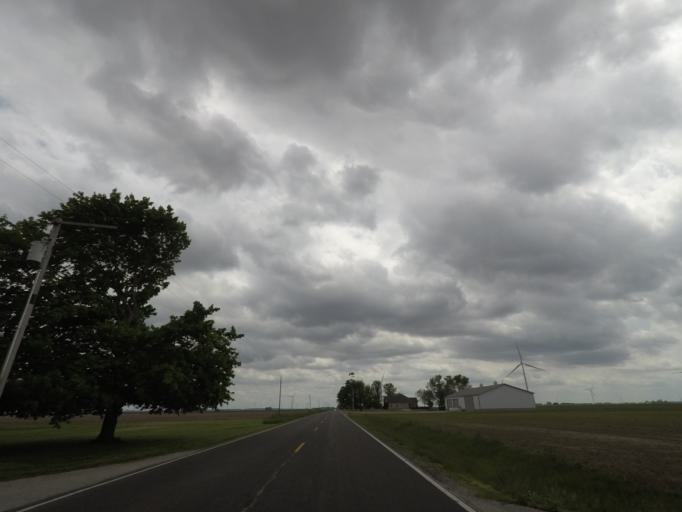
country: US
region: Illinois
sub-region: Macon County
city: Warrensburg
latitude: 40.0248
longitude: -89.0855
